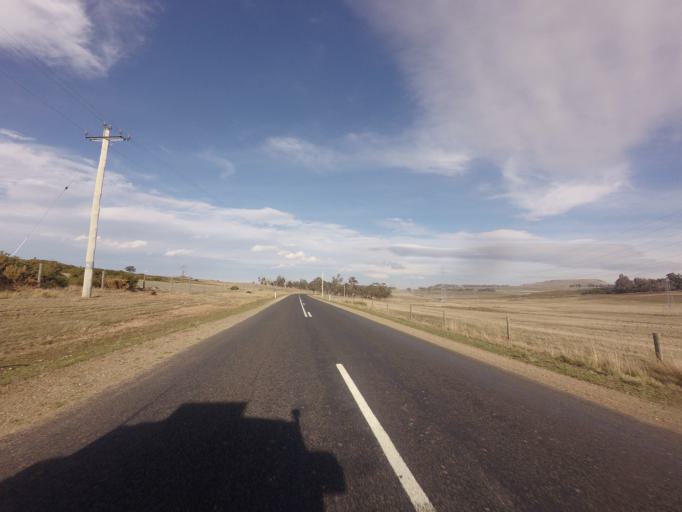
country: AU
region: Tasmania
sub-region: Derwent Valley
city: New Norfolk
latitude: -42.2570
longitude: 146.9361
